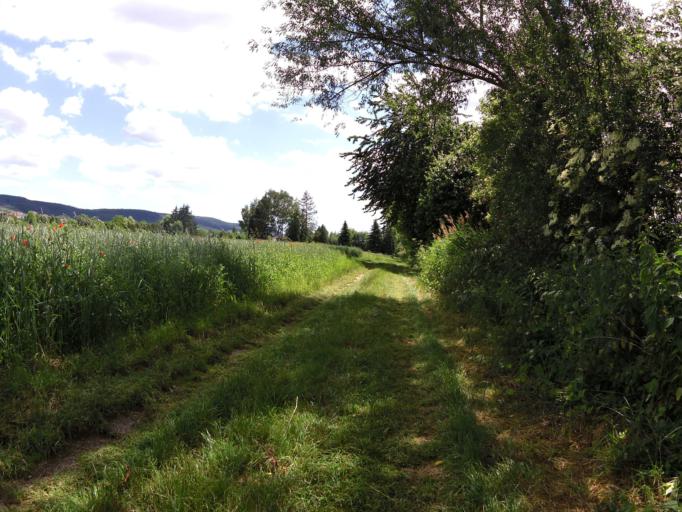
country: DE
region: Bavaria
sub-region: Regierungsbezirk Unterfranken
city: Zellingen
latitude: 49.8882
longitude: 9.8334
